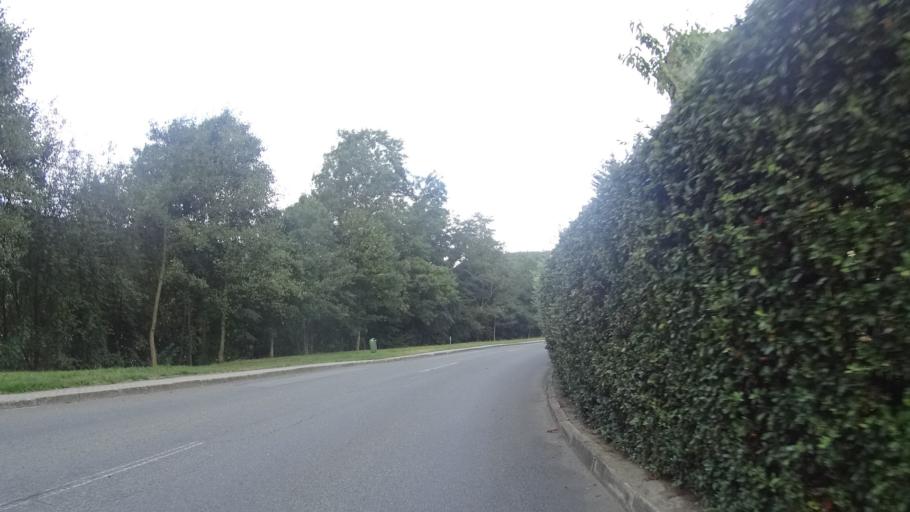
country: CZ
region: Olomoucky
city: Stity
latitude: 49.8735
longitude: 16.7740
